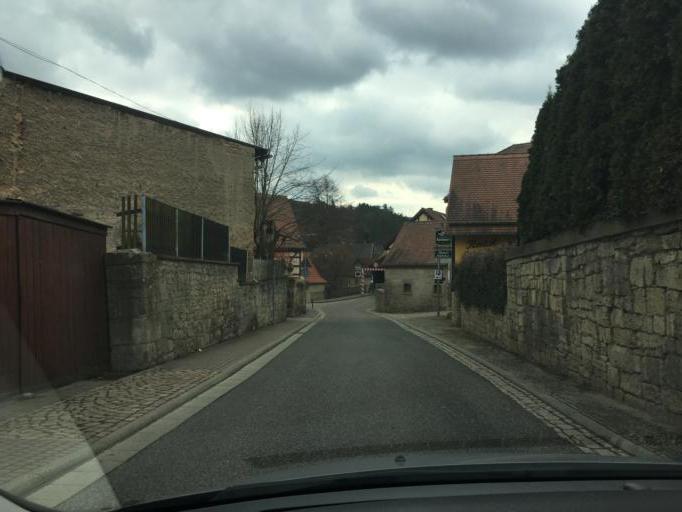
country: DE
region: Thuringia
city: Buchfart
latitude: 50.9221
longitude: 11.3329
